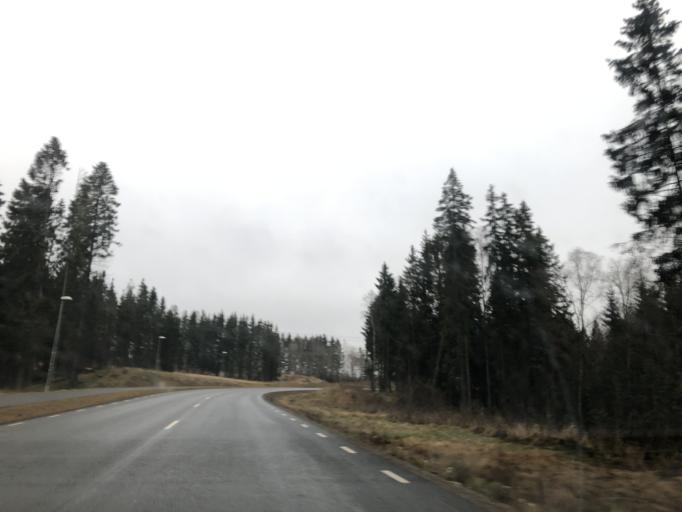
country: SE
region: Vaestra Goetaland
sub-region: Ulricehamns Kommun
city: Ulricehamn
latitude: 57.8163
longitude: 13.2881
